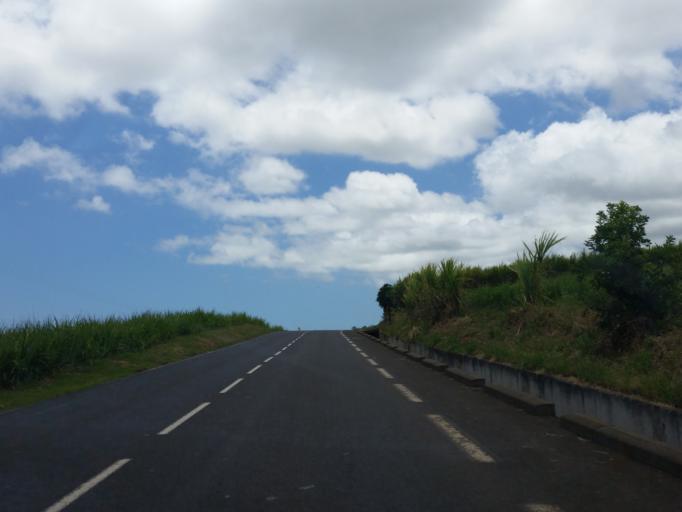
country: RE
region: Reunion
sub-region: Reunion
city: Sainte-Marie
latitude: -20.9167
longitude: 55.5402
